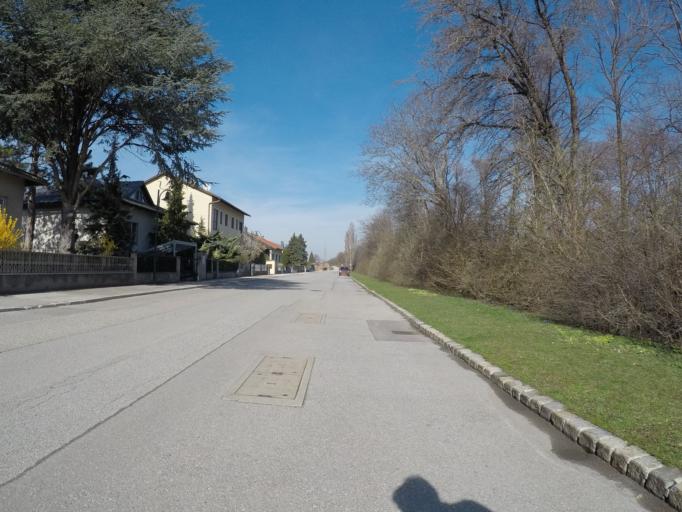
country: AT
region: Lower Austria
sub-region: Politischer Bezirk Modling
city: Vosendorf
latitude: 48.1235
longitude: 16.3417
